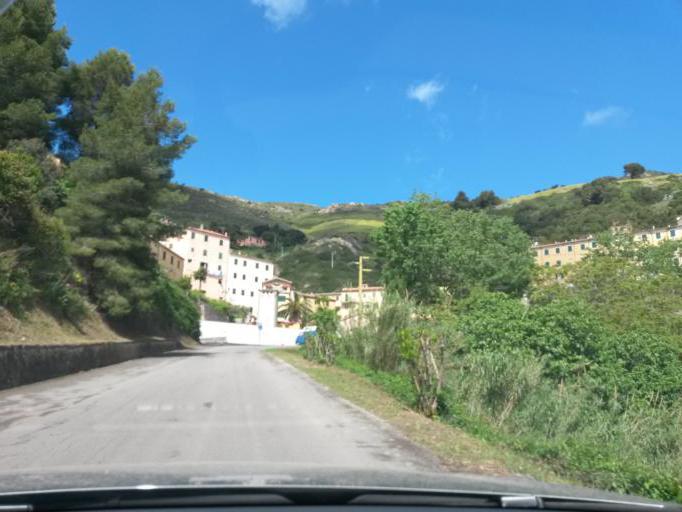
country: IT
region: Tuscany
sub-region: Provincia di Livorno
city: Rio nell'Elba
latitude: 42.8148
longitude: 10.4018
